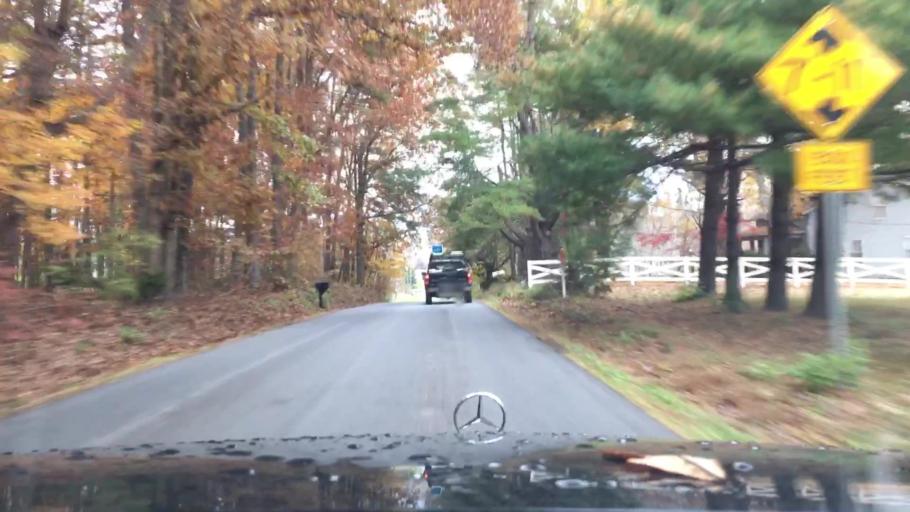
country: US
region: Virginia
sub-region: Campbell County
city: Altavista
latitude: 37.1447
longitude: -79.3056
